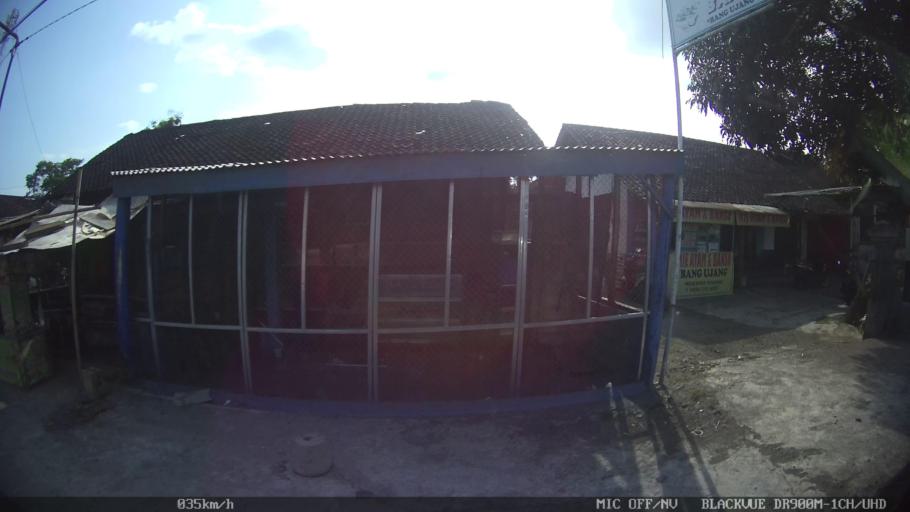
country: ID
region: Central Java
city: Candi Prambanan
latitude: -7.7272
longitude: 110.4723
